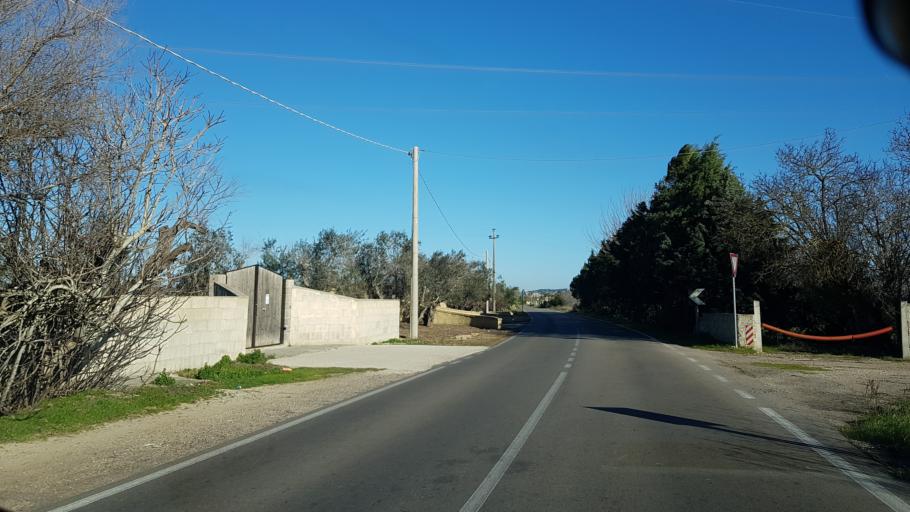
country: IT
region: Apulia
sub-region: Provincia di Lecce
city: Melissano
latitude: 39.9940
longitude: 18.1149
